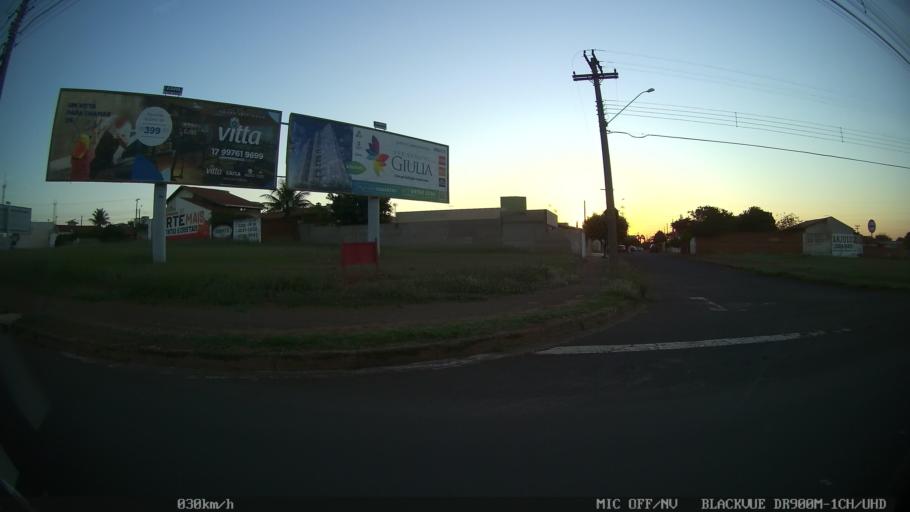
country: BR
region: Sao Paulo
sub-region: Sao Jose Do Rio Preto
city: Sao Jose do Rio Preto
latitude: -20.7971
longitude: -49.3453
